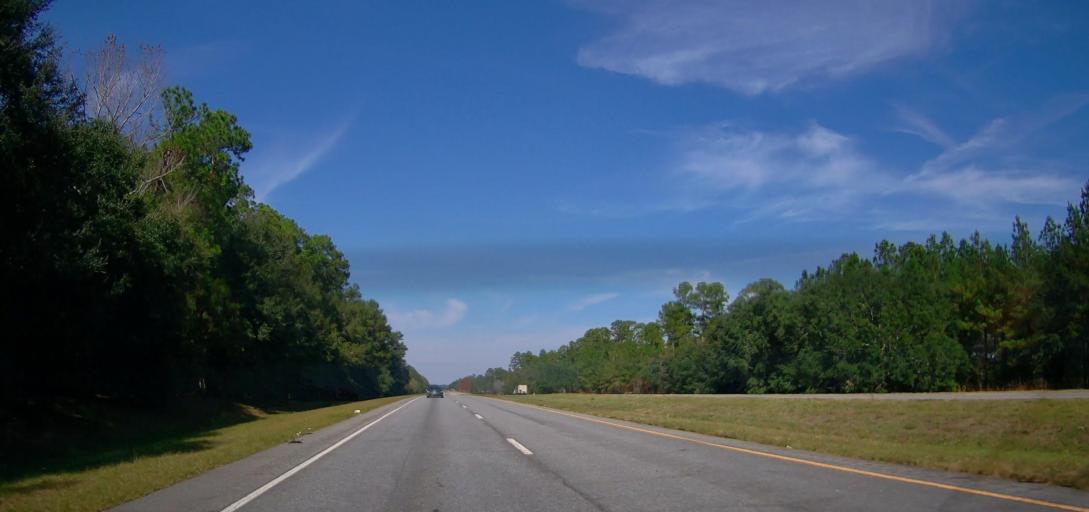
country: US
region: Georgia
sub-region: Lee County
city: Leesburg
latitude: 31.6942
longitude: -83.9925
